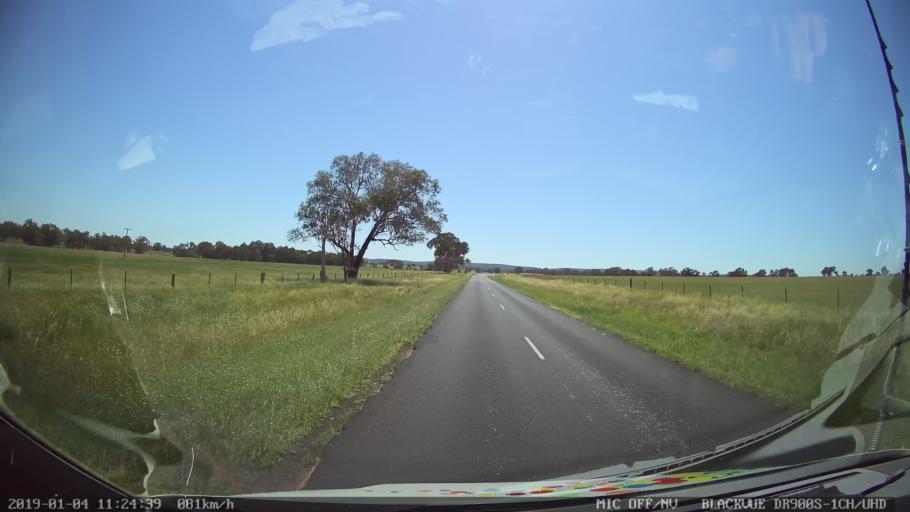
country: AU
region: New South Wales
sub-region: Cabonne
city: Molong
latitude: -33.1313
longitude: 148.7496
